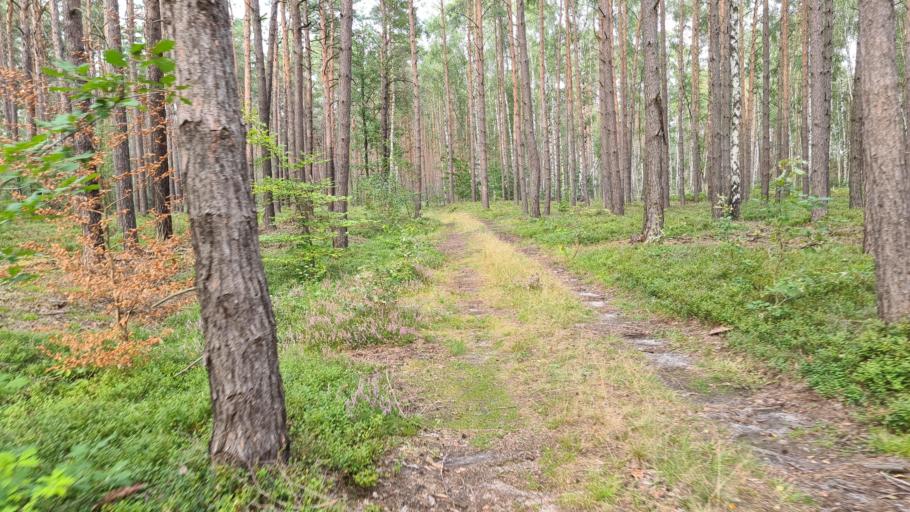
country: DE
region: Brandenburg
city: Trobitz
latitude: 51.6094
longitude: 13.4382
